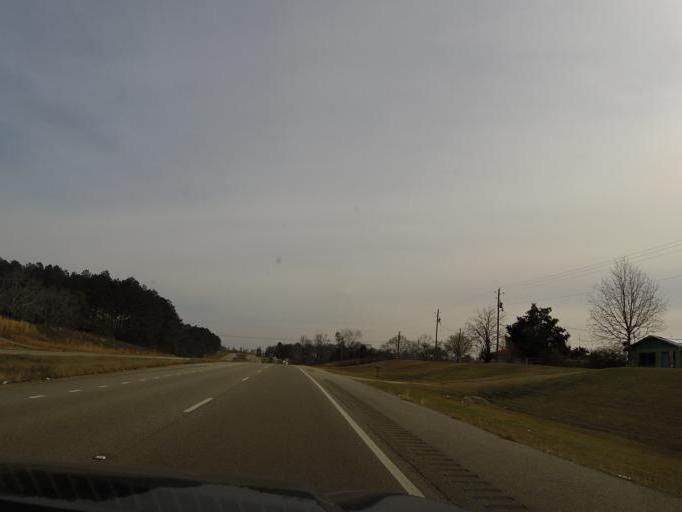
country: US
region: Alabama
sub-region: Houston County
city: Ashford
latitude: 31.1435
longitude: -85.1578
